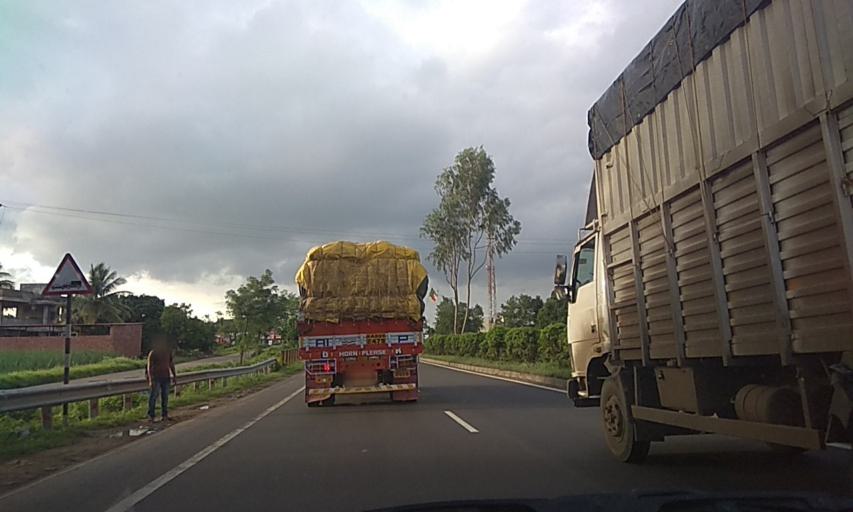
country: IN
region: Maharashtra
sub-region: Satara Division
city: Rahimatpur
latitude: 17.4819
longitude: 74.0855
